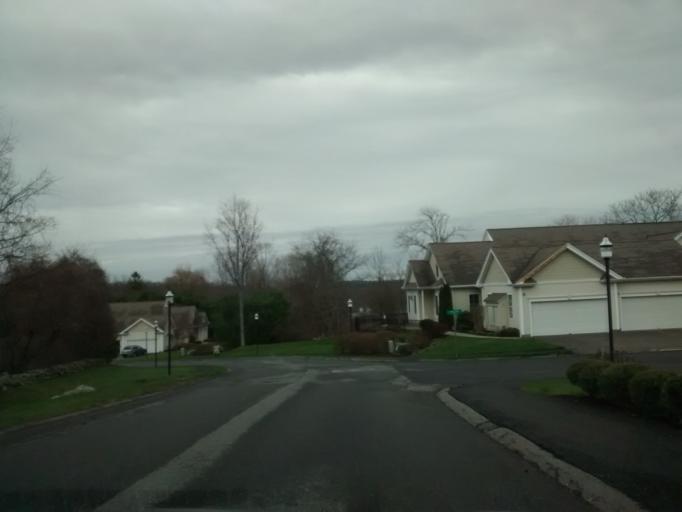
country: US
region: Massachusetts
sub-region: Worcester County
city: Grafton
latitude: 42.2457
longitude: -71.7158
